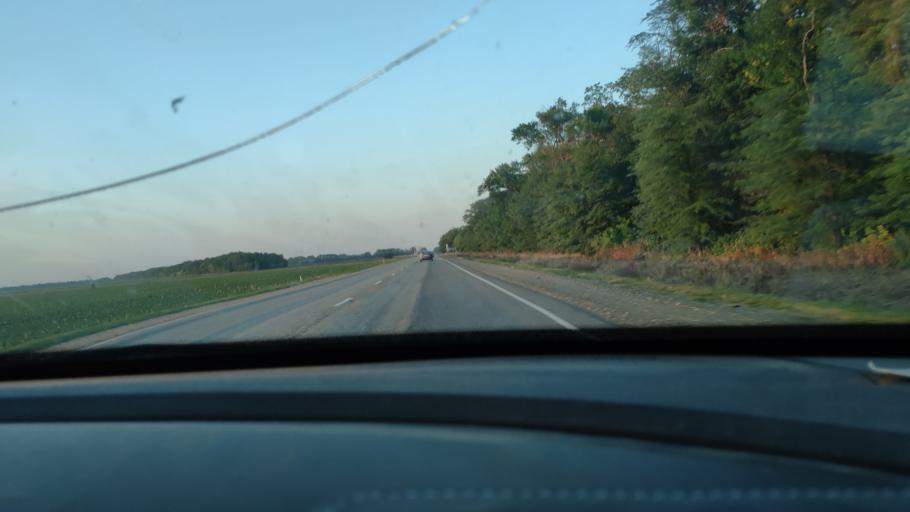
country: RU
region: Krasnodarskiy
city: Starominskaya
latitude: 46.4600
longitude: 39.0366
